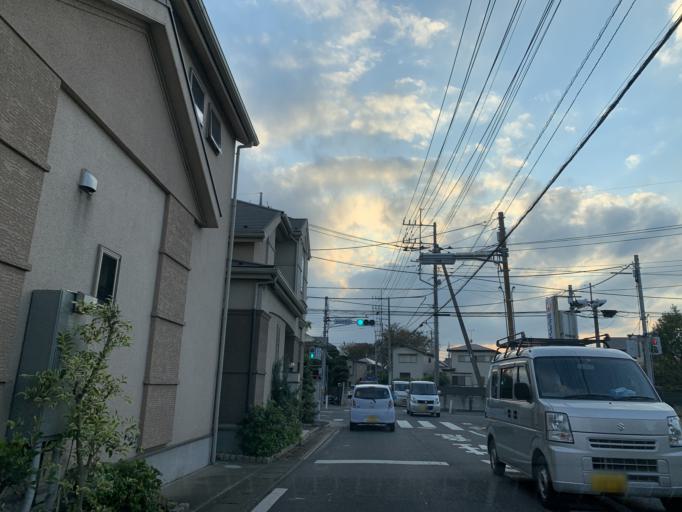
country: JP
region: Chiba
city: Nagareyama
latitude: 35.8936
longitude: 139.9152
